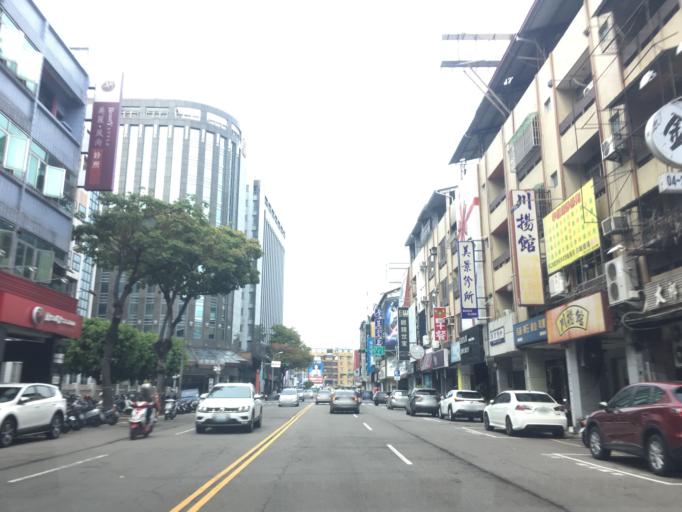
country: TW
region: Taiwan
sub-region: Taichung City
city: Taichung
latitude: 24.1575
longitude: 120.6549
